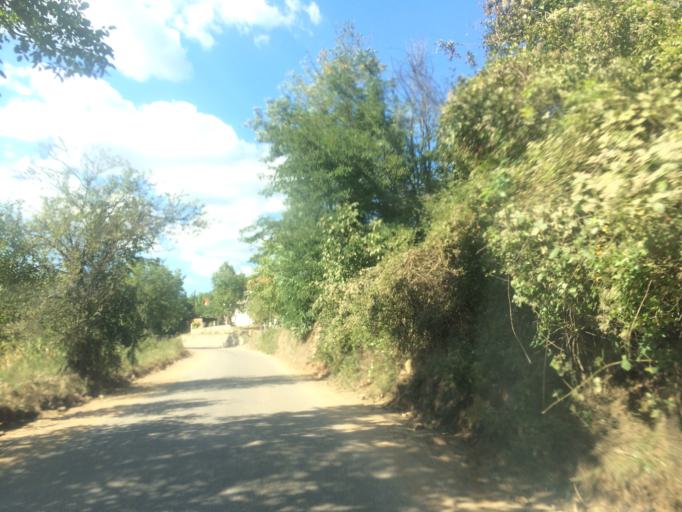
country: MK
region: Makedonska Kamenica
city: Makedonska Kamenica
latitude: 42.0397
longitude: 22.5790
